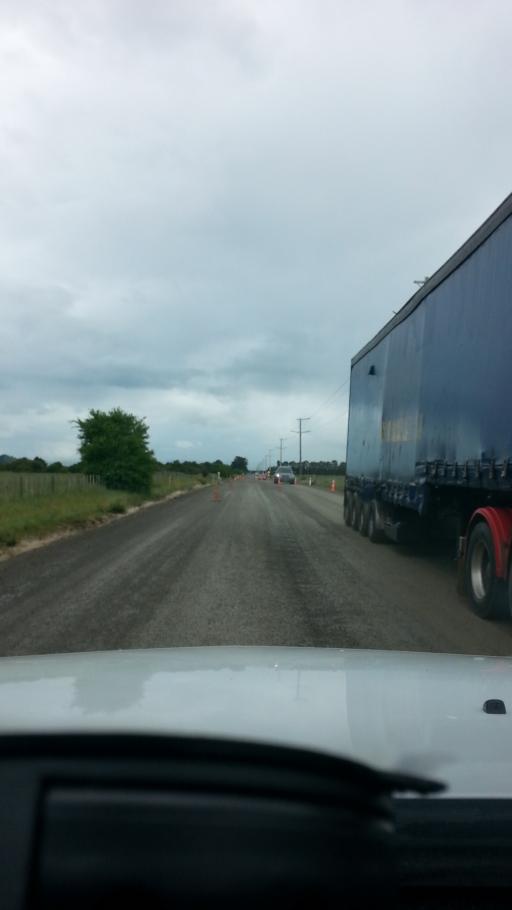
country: NZ
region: Wellington
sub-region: Masterton District
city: Masterton
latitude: -40.8280
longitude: 175.6262
